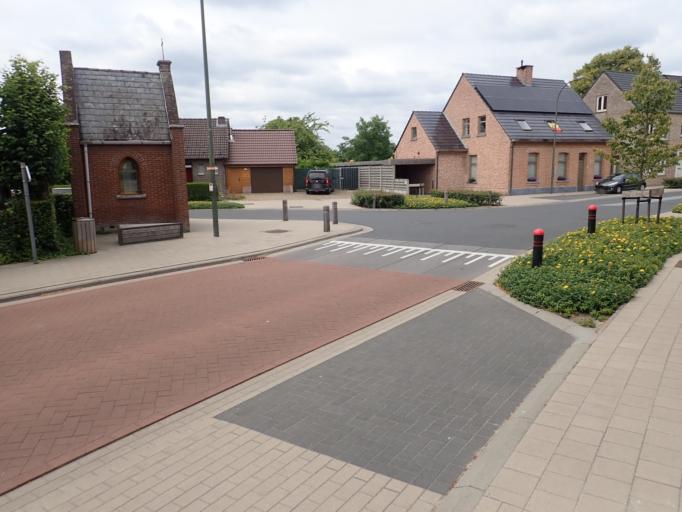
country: BE
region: Flanders
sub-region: Provincie Antwerpen
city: Baarle-Hertog
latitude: 51.4036
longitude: 4.8916
